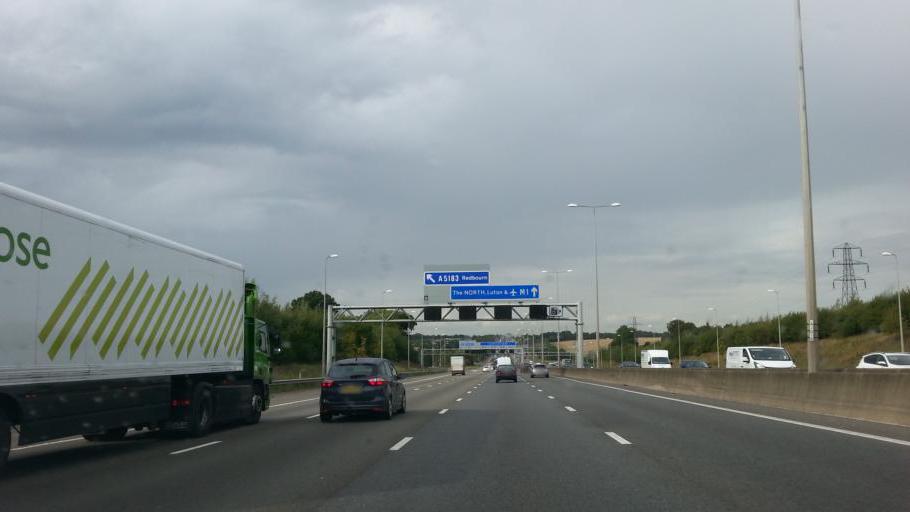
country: GB
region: England
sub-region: Hertfordshire
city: Flamstead
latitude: 51.8147
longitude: -0.4163
